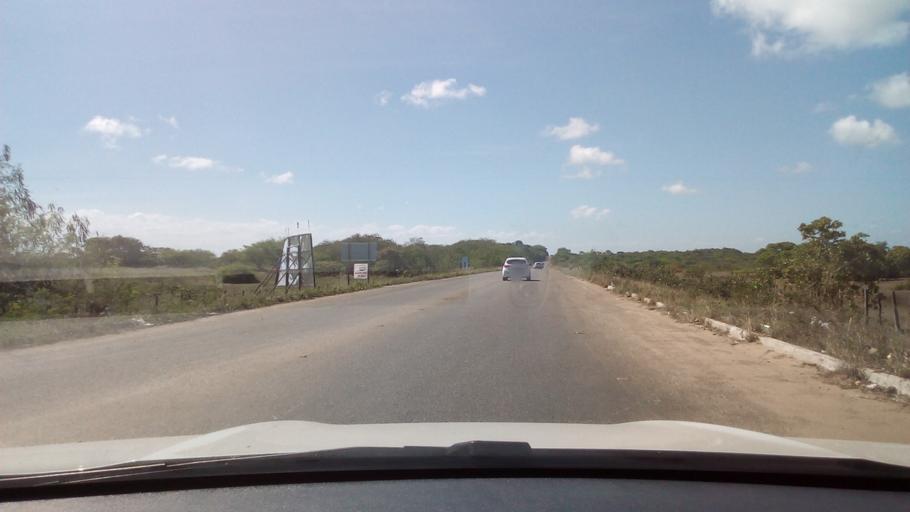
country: BR
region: Rio Grande do Norte
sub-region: Ares
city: Ares
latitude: -6.2330
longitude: -35.0739
